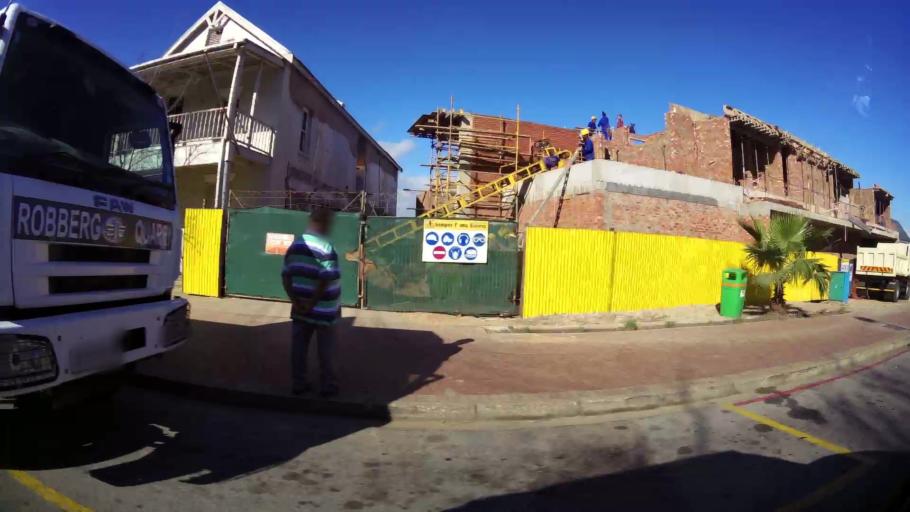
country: ZA
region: Western Cape
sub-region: Eden District Municipality
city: Knysna
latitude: -34.0348
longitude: 23.0443
